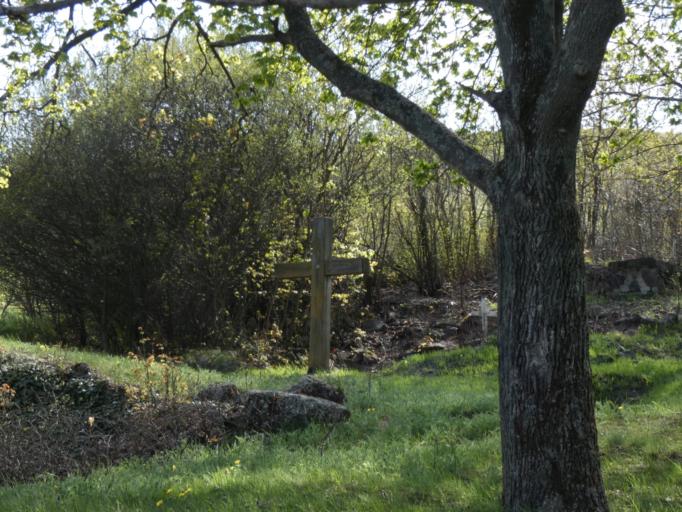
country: HU
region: Nograd
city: Bujak
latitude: 47.8905
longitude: 19.6029
